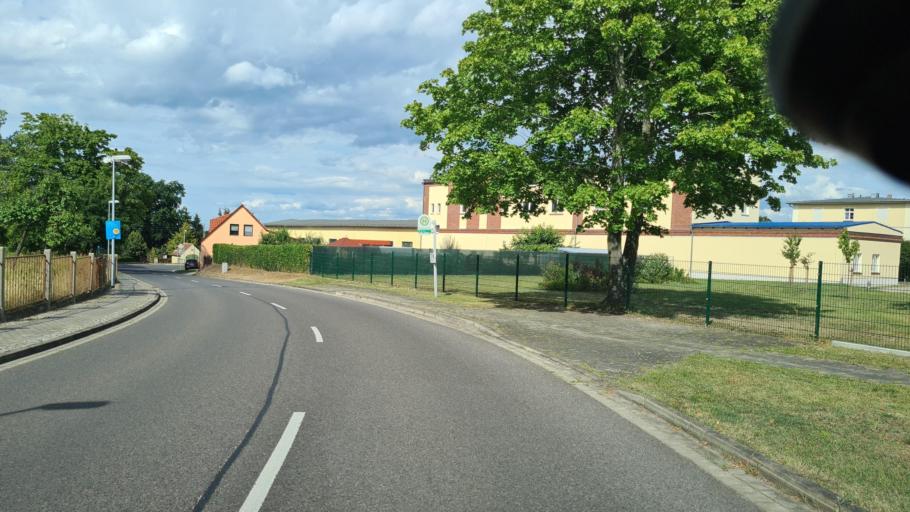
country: DE
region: Brandenburg
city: Neupetershain
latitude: 51.6246
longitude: 14.1613
